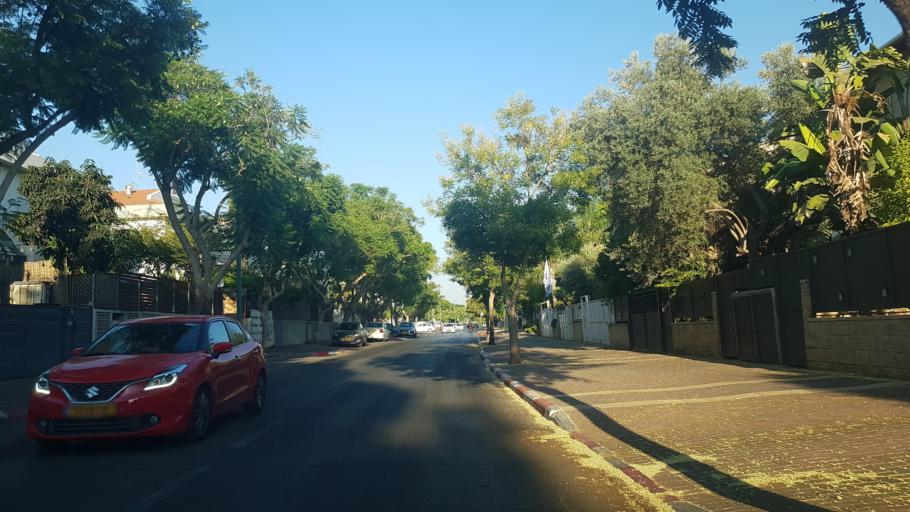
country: IL
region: Central District
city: Kfar Saba
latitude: 32.1823
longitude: 34.9324
